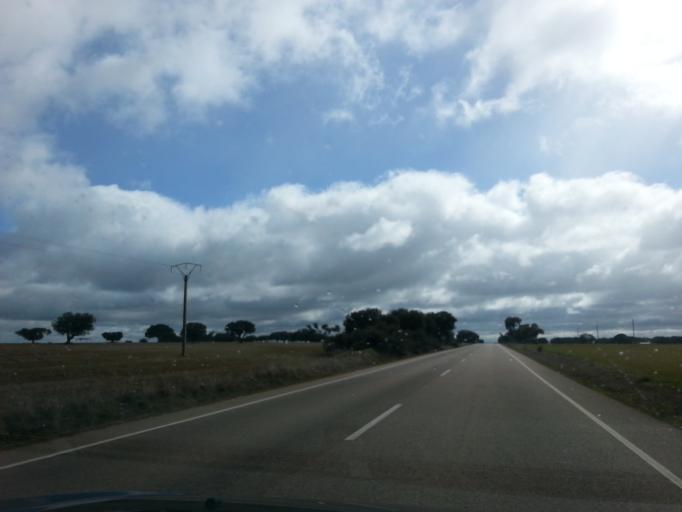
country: ES
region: Castille and Leon
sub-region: Provincia de Salamanca
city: Cabrillas
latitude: 40.7594
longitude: -6.1989
